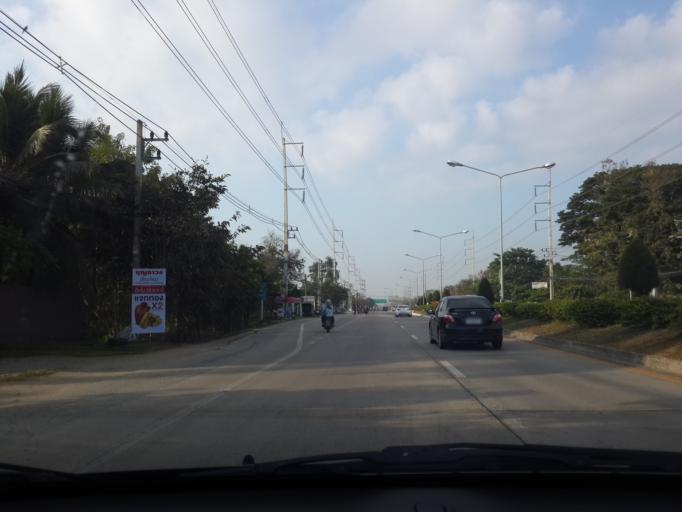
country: TH
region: Chiang Mai
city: San Sai
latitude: 18.8302
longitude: 99.0528
